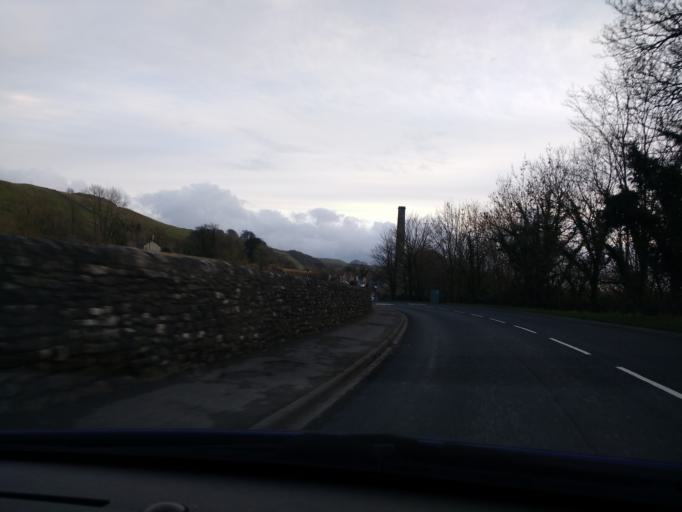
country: GB
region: England
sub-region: North Yorkshire
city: Settle
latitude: 54.0760
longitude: -2.2786
